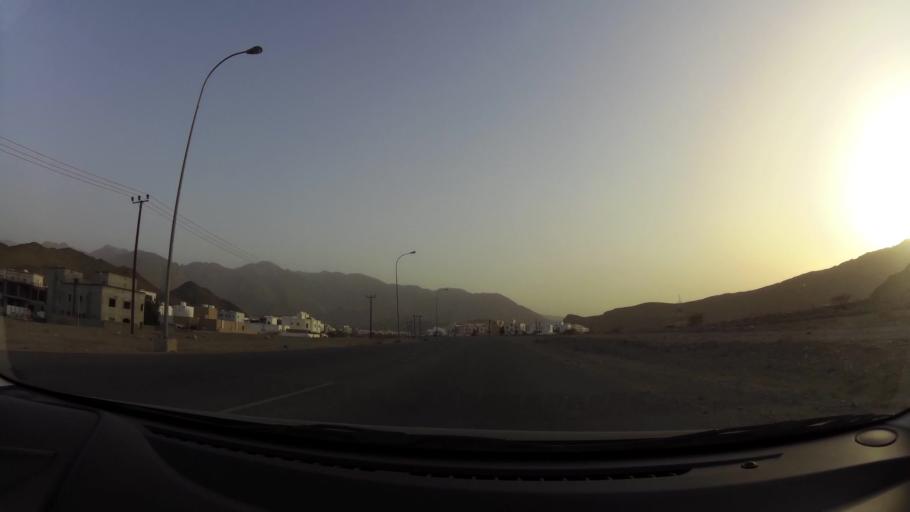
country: OM
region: Muhafazat Masqat
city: Bawshar
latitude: 23.4888
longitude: 58.3154
